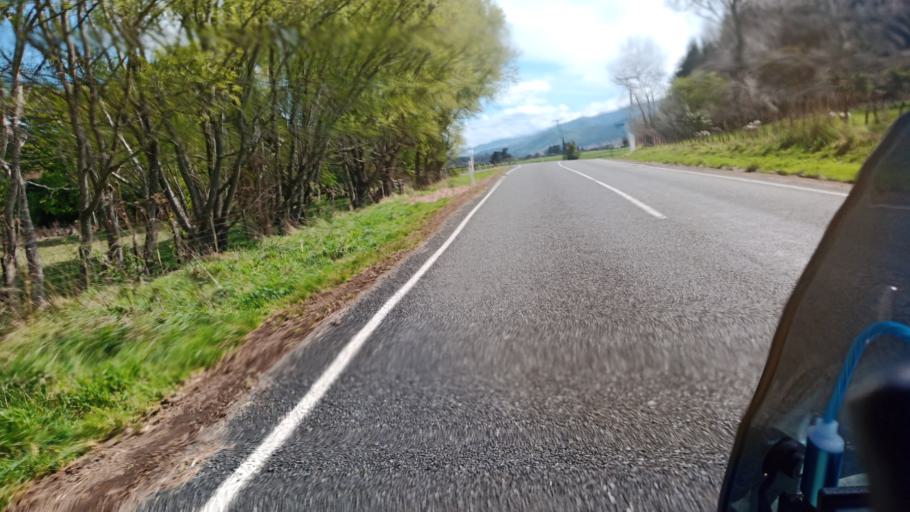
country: NZ
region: Gisborne
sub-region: Gisborne District
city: Gisborne
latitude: -37.8799
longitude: 178.2948
